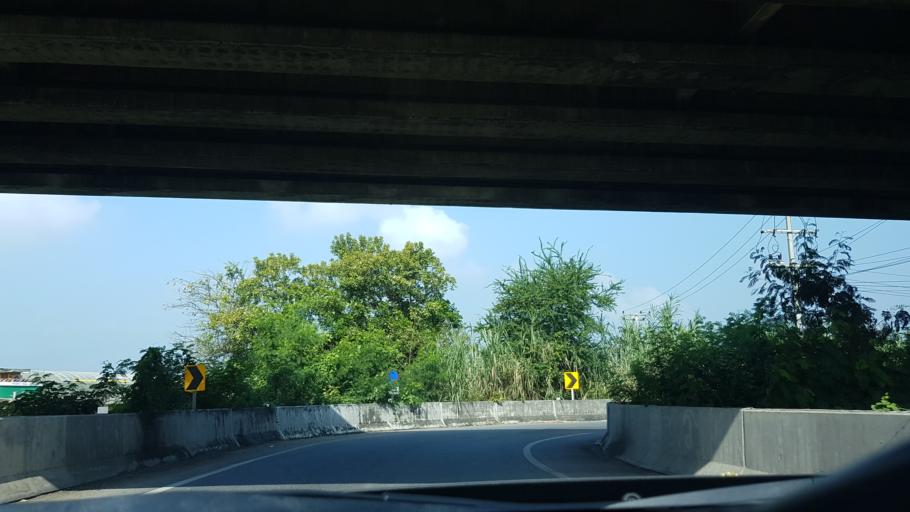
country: TH
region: Pathum Thani
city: Sam Khok
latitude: 14.1196
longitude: 100.5356
